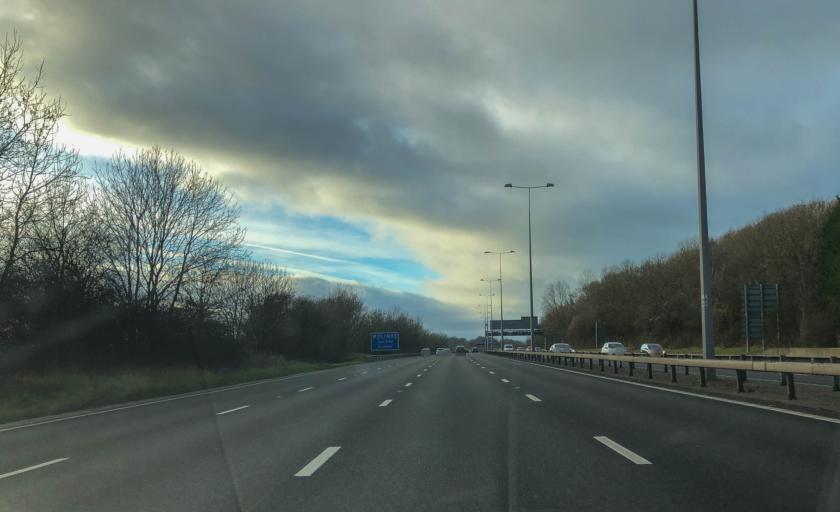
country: GB
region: England
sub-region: Surrey
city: Godstone
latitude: 51.2577
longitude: -0.0811
